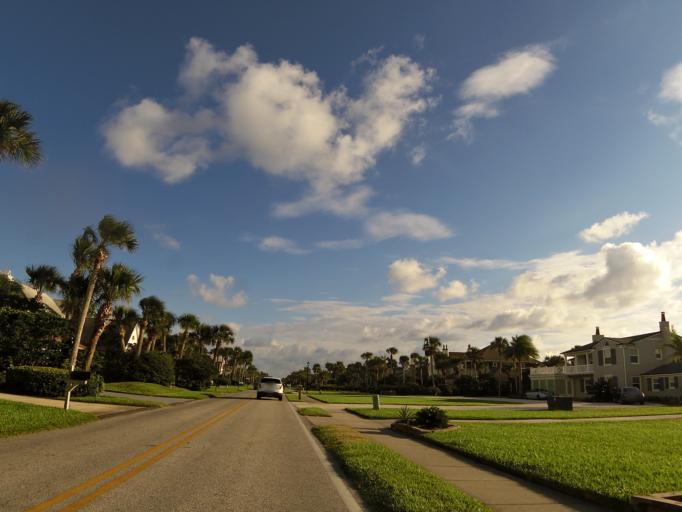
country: US
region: Florida
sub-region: Saint Johns County
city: Ponte Vedra Beach
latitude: 30.2340
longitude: -81.3765
